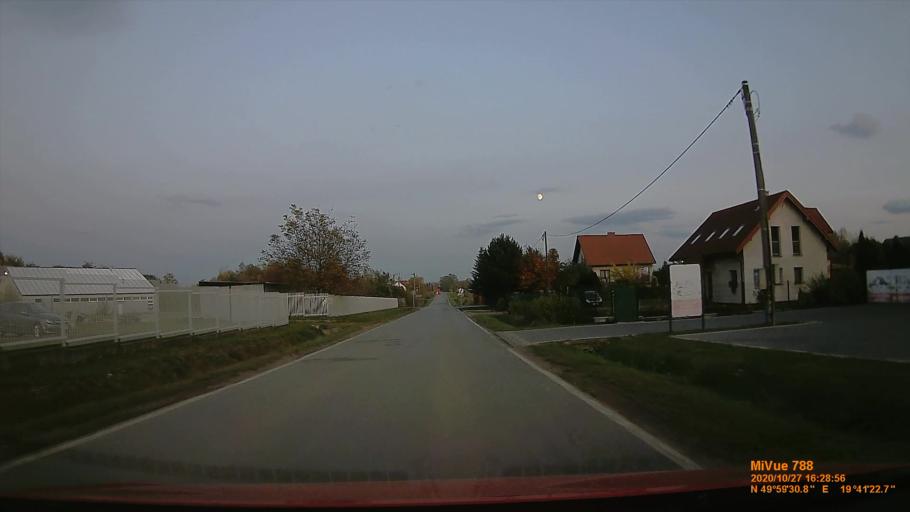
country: PL
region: Lesser Poland Voivodeship
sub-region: Powiat krakowski
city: Czernichow
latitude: 49.9919
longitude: 19.6896
